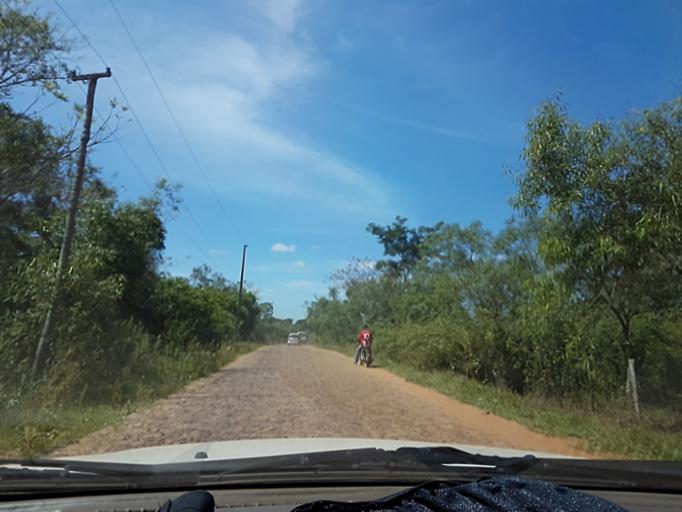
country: PY
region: Cordillera
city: Arroyos y Esteros
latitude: -24.9863
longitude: -57.2080
